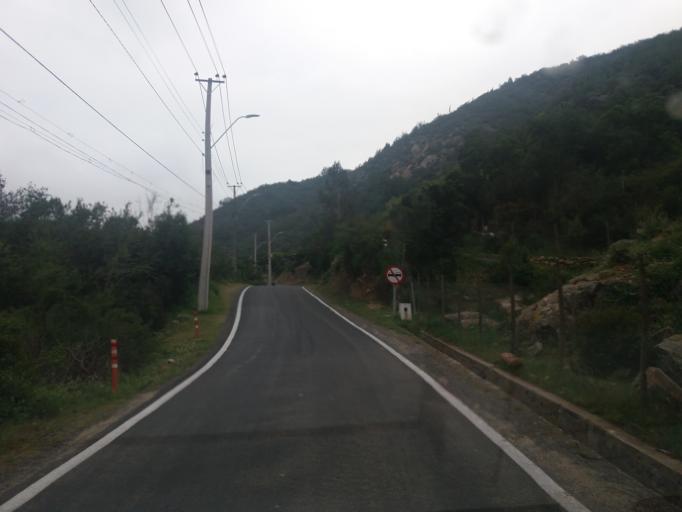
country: CL
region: Valparaiso
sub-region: Provincia de Marga Marga
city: Limache
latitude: -33.0364
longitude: -71.0913
